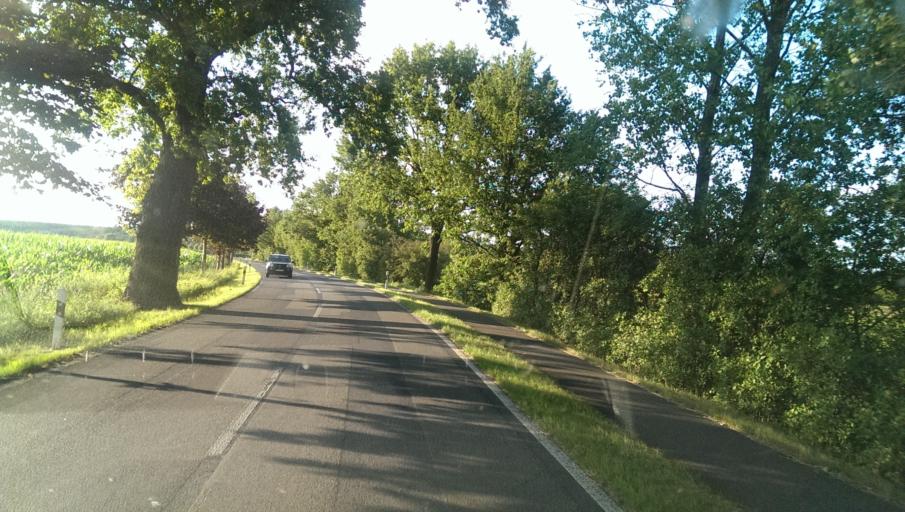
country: DE
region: Brandenburg
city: Trebbin
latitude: 52.2290
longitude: 13.1968
